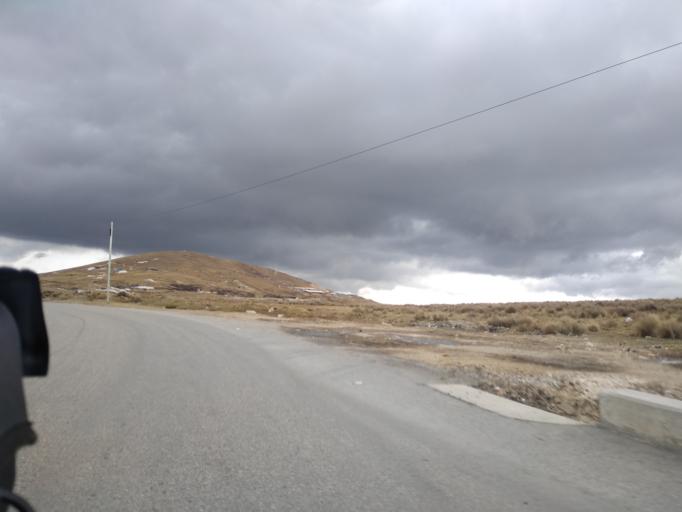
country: PE
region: La Libertad
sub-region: Provincia de Santiago de Chuco
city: Quiruvilca
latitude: -7.9909
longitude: -78.2914
